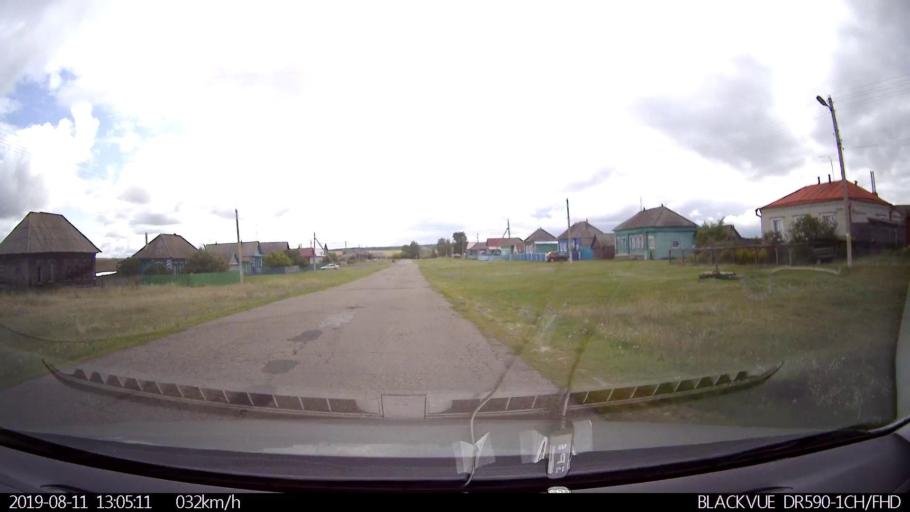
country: RU
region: Ulyanovsk
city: Ignatovka
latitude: 53.8719
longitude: 47.6492
